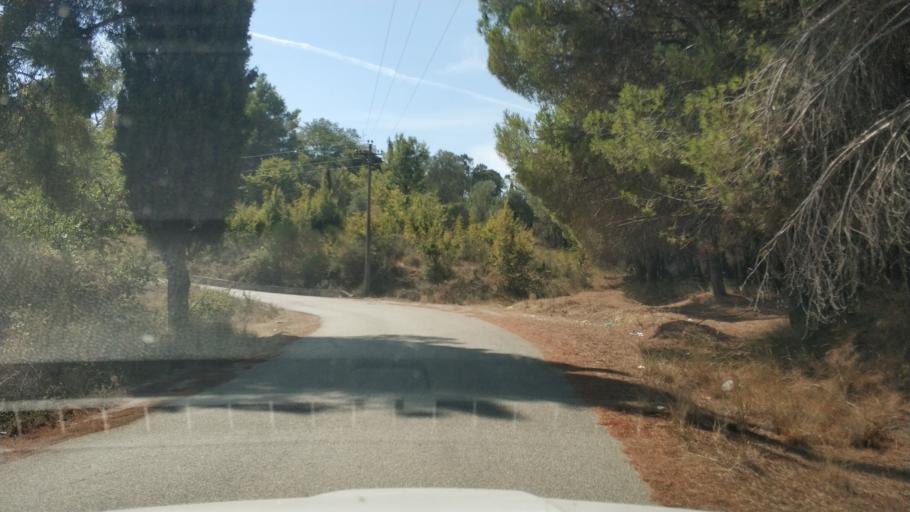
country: AL
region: Fier
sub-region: Rrethi i Lushnjes
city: Kolonje
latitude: 40.8201
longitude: 19.5941
